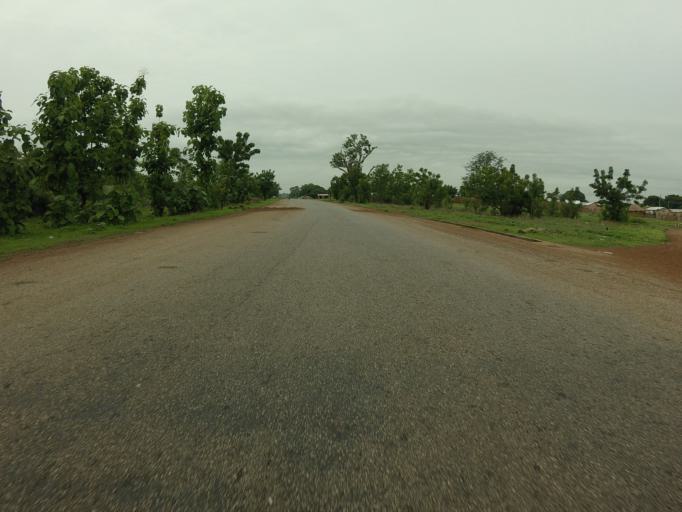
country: GH
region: Northern
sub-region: Yendi
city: Yendi
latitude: 9.5054
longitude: -0.0272
